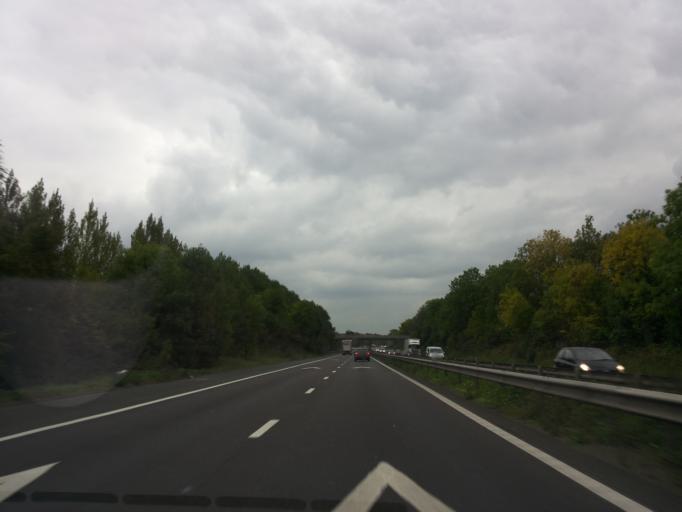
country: GB
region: England
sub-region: Kent
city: Teynham
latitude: 51.2974
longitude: 0.7751
